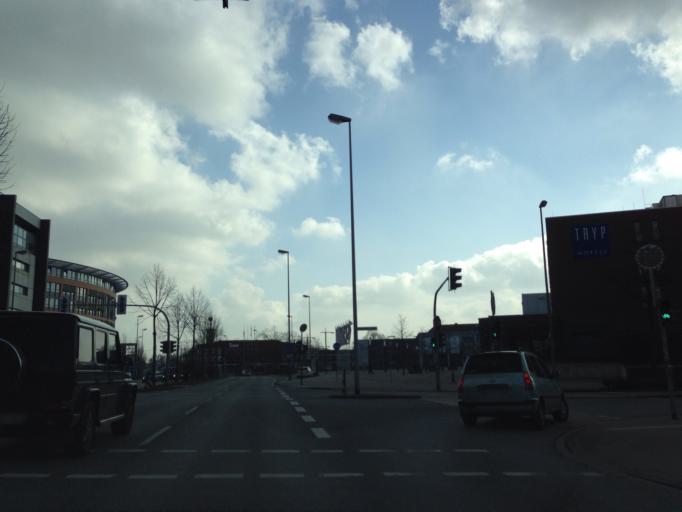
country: DE
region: North Rhine-Westphalia
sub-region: Regierungsbezirk Munster
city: Muenster
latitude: 51.9501
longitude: 7.6378
